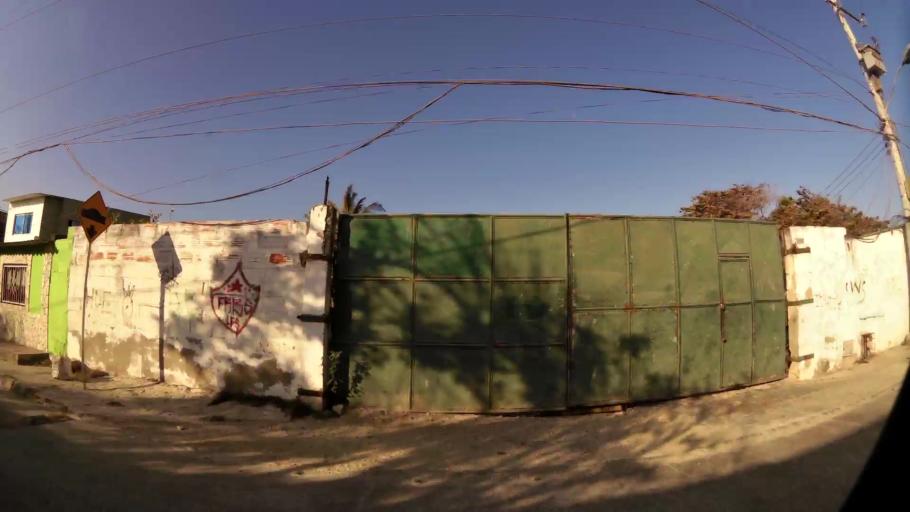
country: CO
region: Atlantico
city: Barranquilla
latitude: 11.0421
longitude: -74.8251
